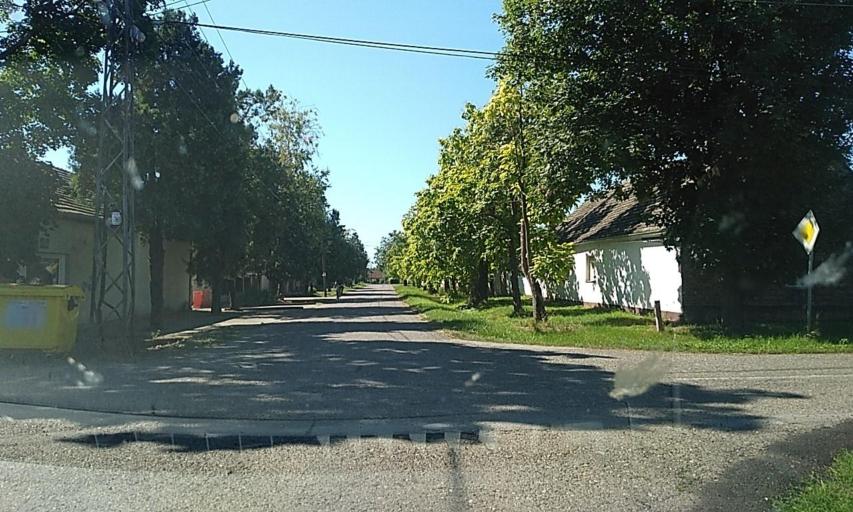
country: RS
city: Backo Gradiste
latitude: 45.5315
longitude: 20.0267
